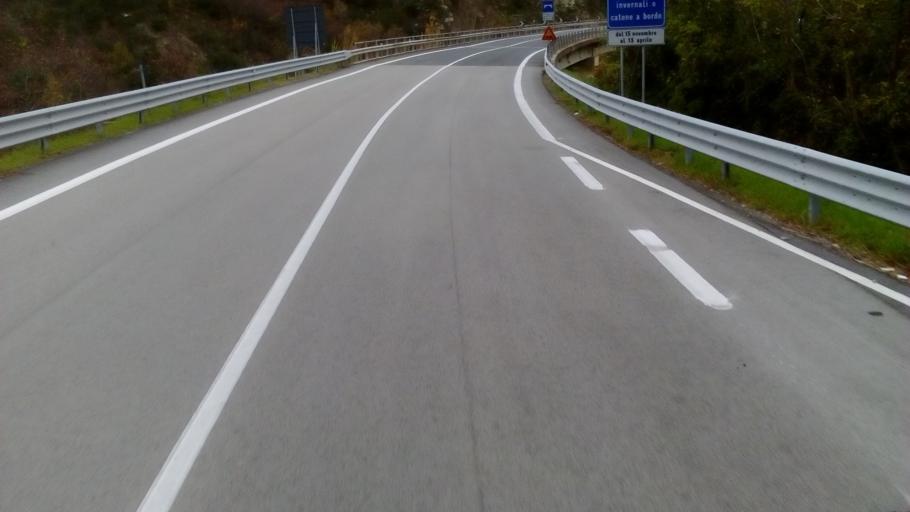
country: IT
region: Molise
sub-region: Provincia di Campobasso
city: Trivento
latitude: 41.7907
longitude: 14.5380
